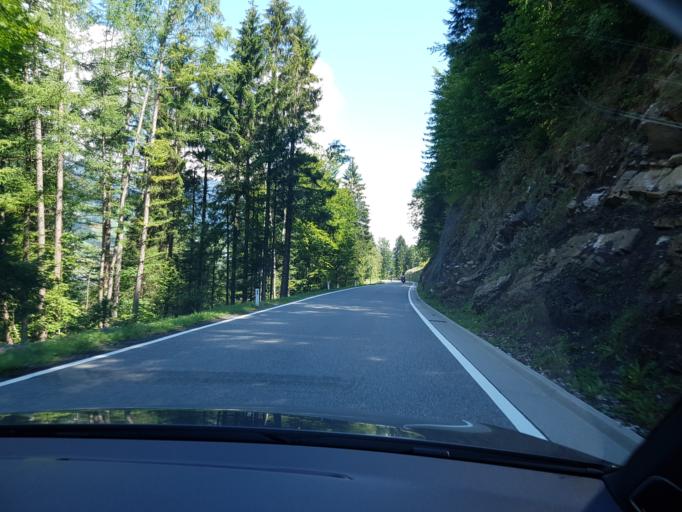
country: AT
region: Vorarlberg
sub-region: Politischer Bezirk Bludenz
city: Ludesch
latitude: 47.2082
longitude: 9.8007
